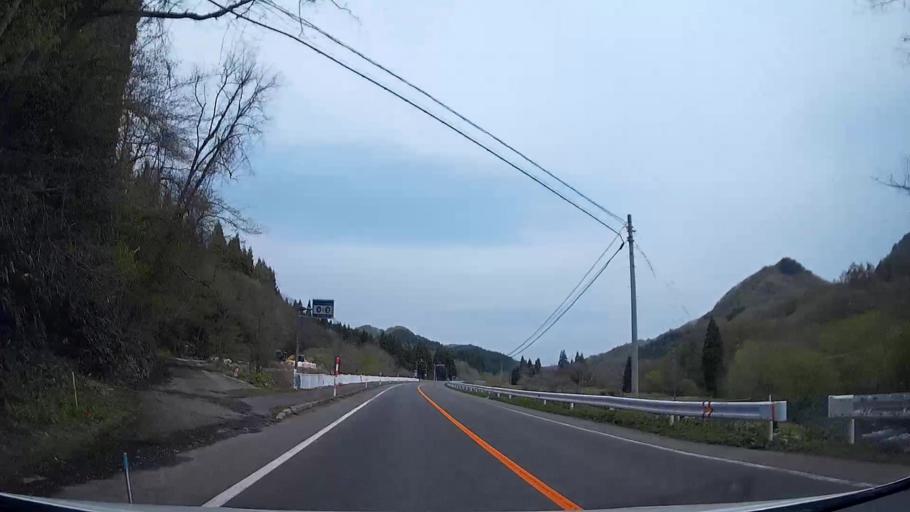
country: JP
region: Akita
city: Hanawa
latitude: 40.3680
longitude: 140.8659
